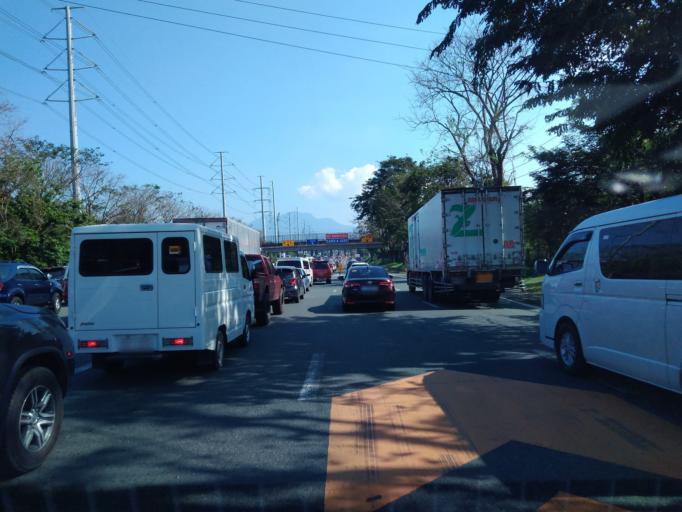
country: PH
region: Calabarzon
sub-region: Province of Laguna
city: Prinza
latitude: 14.2225
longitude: 121.1230
